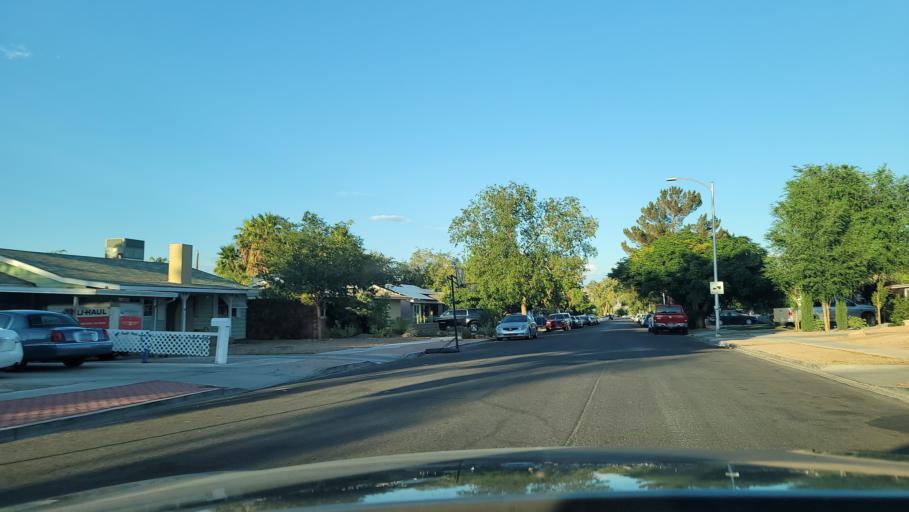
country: US
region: Nevada
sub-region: Clark County
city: Las Vegas
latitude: 36.1568
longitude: -115.1233
